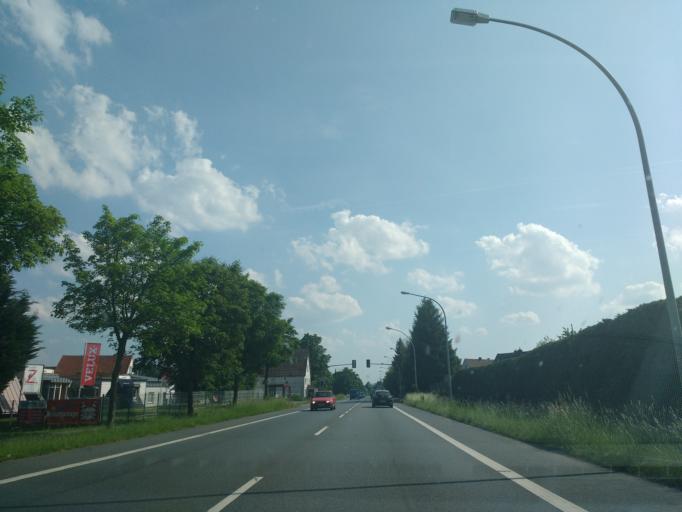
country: DE
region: North Rhine-Westphalia
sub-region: Regierungsbezirk Detmold
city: Bad Salzuflen
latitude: 52.0435
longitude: 8.7583
